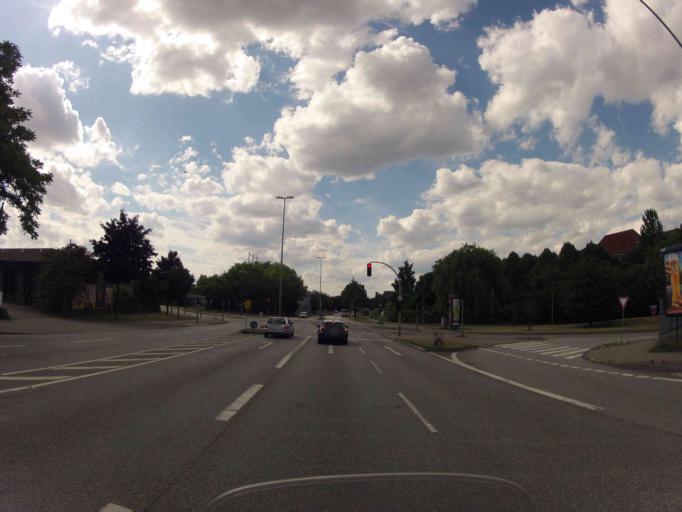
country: DE
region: Hamburg
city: Rothenburgsort
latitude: 53.5407
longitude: 10.0486
